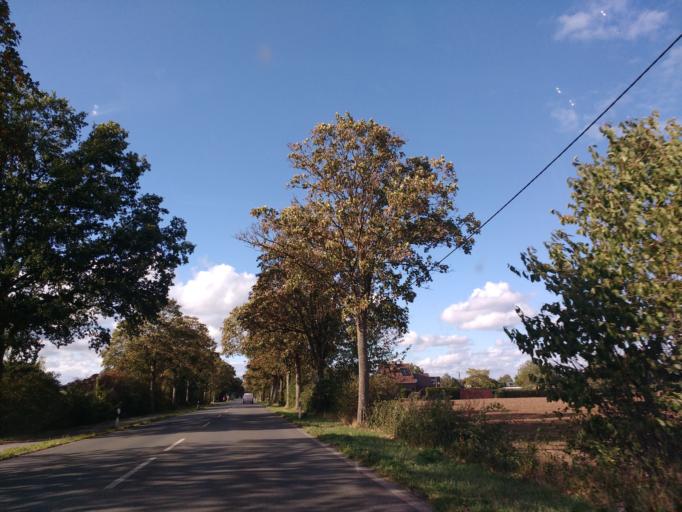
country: DE
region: North Rhine-Westphalia
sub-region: Regierungsbezirk Dusseldorf
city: Alpen
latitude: 51.6009
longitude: 6.5266
